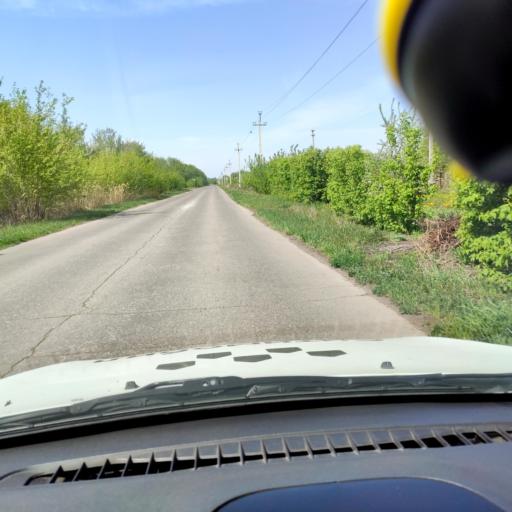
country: RU
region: Samara
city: Tol'yatti
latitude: 53.6641
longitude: 49.3510
